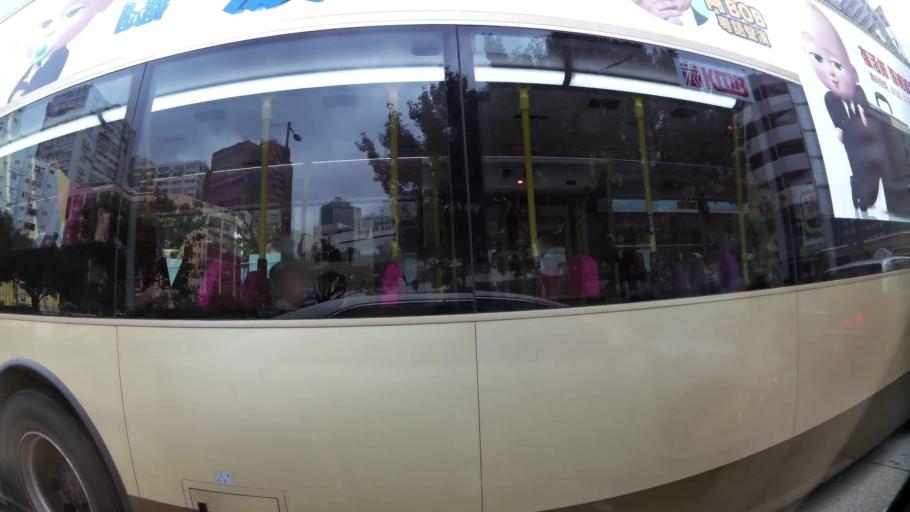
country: HK
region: Wong Tai Sin
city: Wong Tai Sin
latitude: 22.3379
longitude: 114.2021
